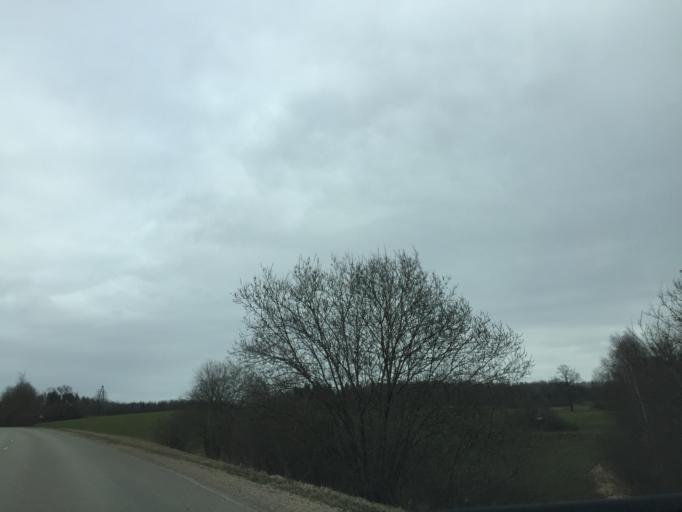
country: LV
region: Kraslavas Rajons
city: Kraslava
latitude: 55.9338
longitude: 27.1568
